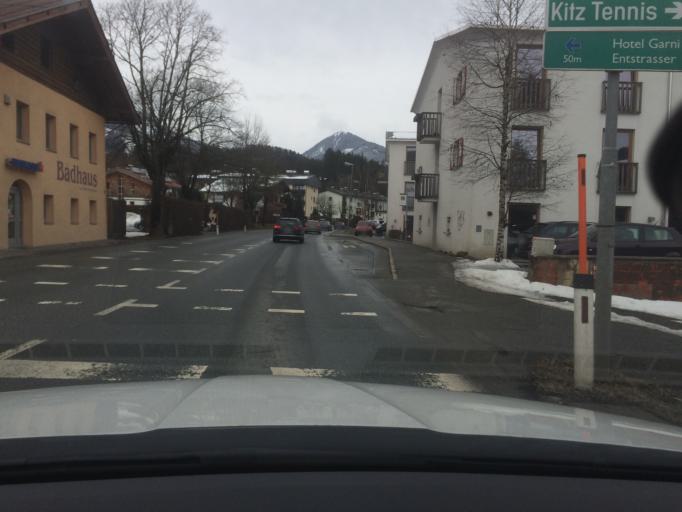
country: AT
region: Tyrol
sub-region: Politischer Bezirk Kitzbuhel
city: Kitzbuhel
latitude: 47.4367
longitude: 12.4042
